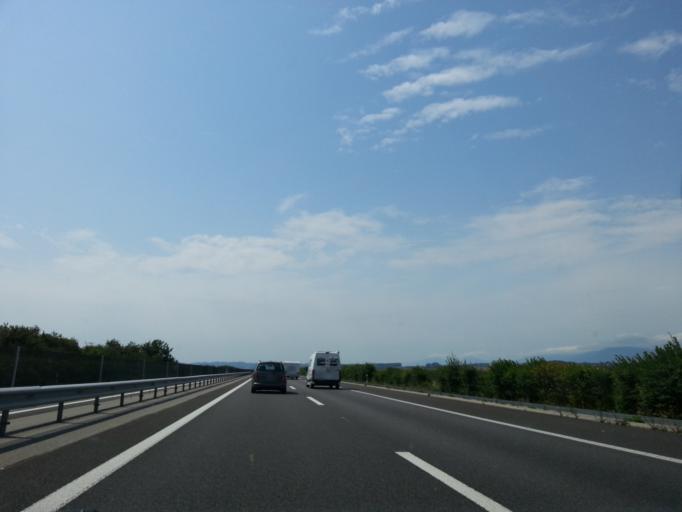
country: CH
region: Fribourg
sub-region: Broye District
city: Domdidier
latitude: 46.8684
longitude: 6.9723
